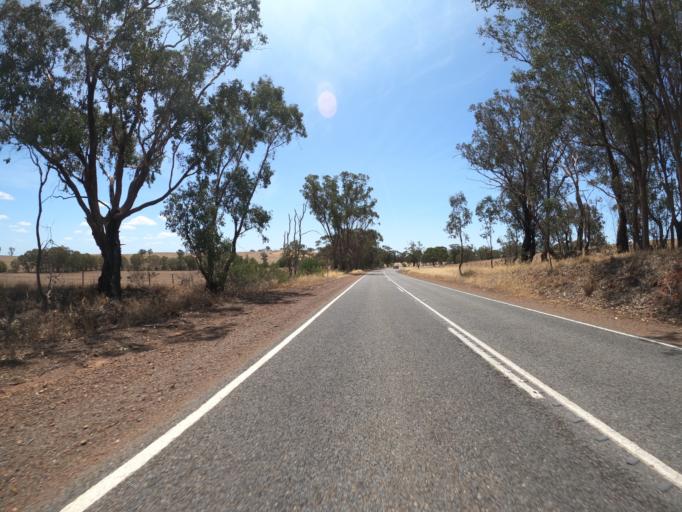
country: AU
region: Victoria
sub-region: Benalla
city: Benalla
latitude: -36.3367
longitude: 145.9590
